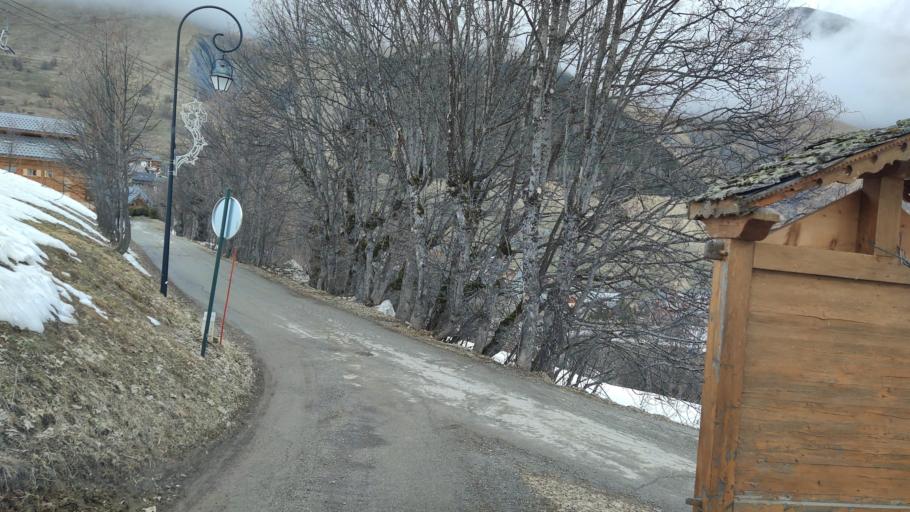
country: FR
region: Rhone-Alpes
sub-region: Departement de la Savoie
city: Saint-Jean-de-Maurienne
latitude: 45.2168
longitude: 6.2255
